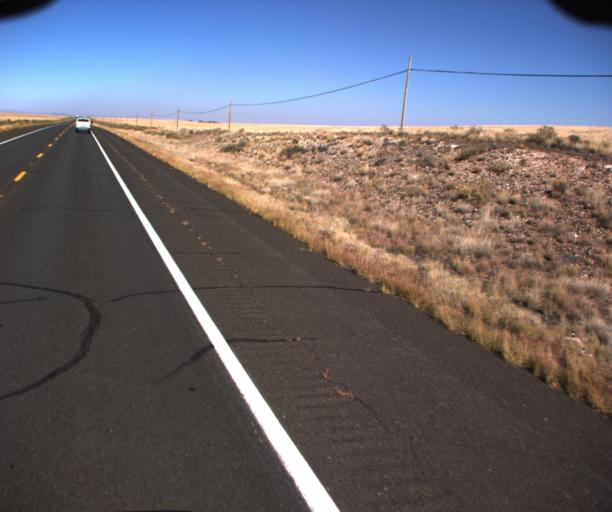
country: US
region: Arizona
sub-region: Coconino County
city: Flagstaff
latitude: 35.6093
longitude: -111.5241
